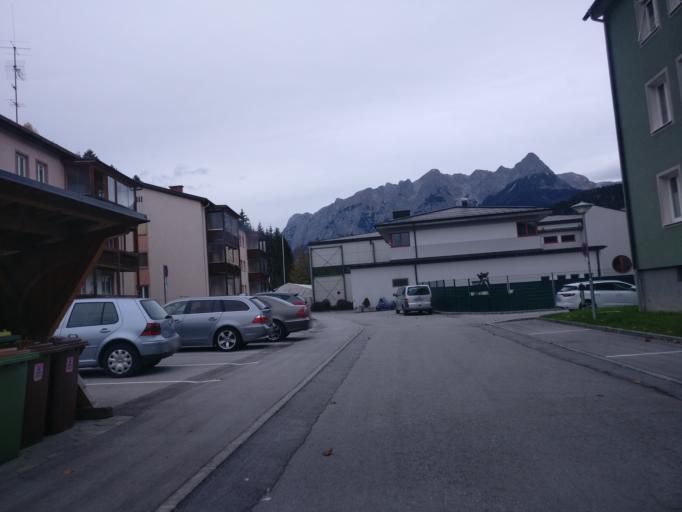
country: AT
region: Salzburg
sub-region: Politischer Bezirk Sankt Johann im Pongau
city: Bischofshofen
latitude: 47.4254
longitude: 13.2148
